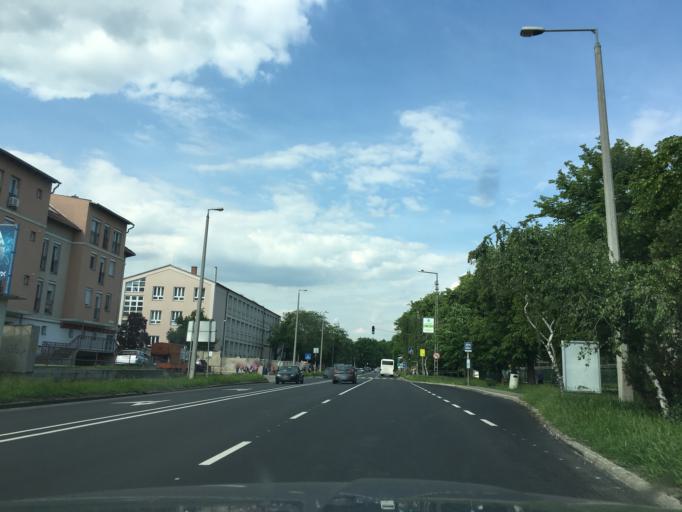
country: HU
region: Hajdu-Bihar
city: Debrecen
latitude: 47.5216
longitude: 21.6173
